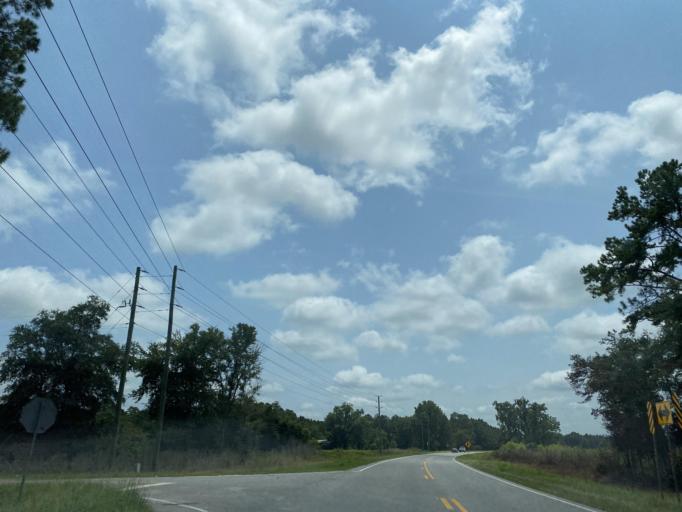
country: US
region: Georgia
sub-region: Jeff Davis County
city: Hazlehurst
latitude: 31.8072
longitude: -82.5658
